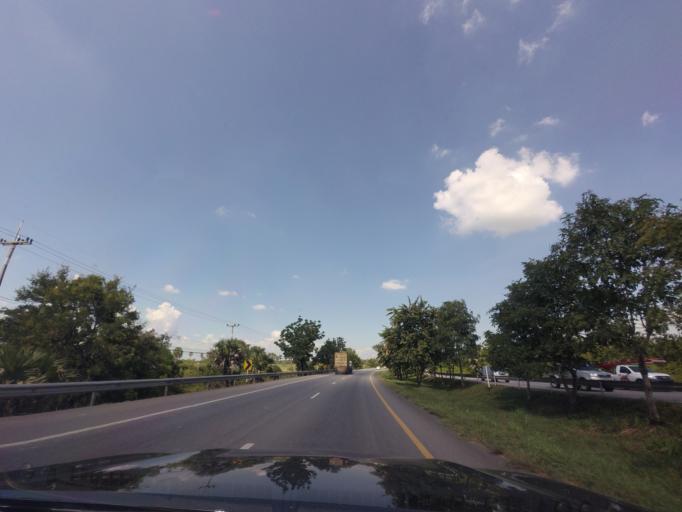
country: TH
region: Nakhon Ratchasima
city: Non Sung
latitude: 15.1388
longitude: 102.3124
